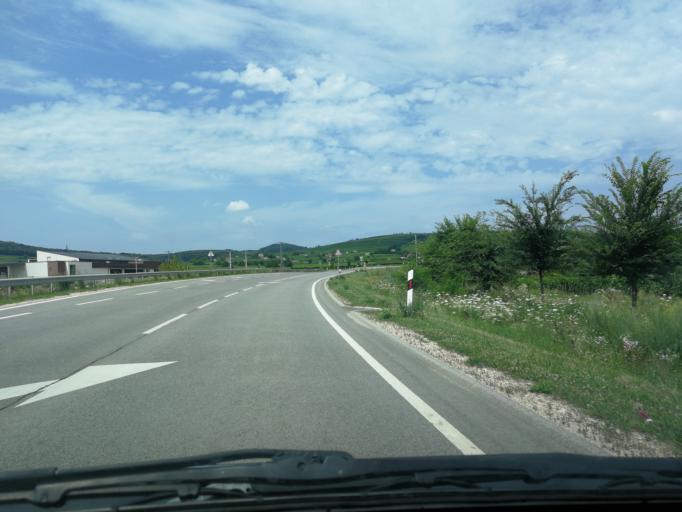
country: HU
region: Baranya
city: Villany
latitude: 45.8602
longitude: 18.4450
